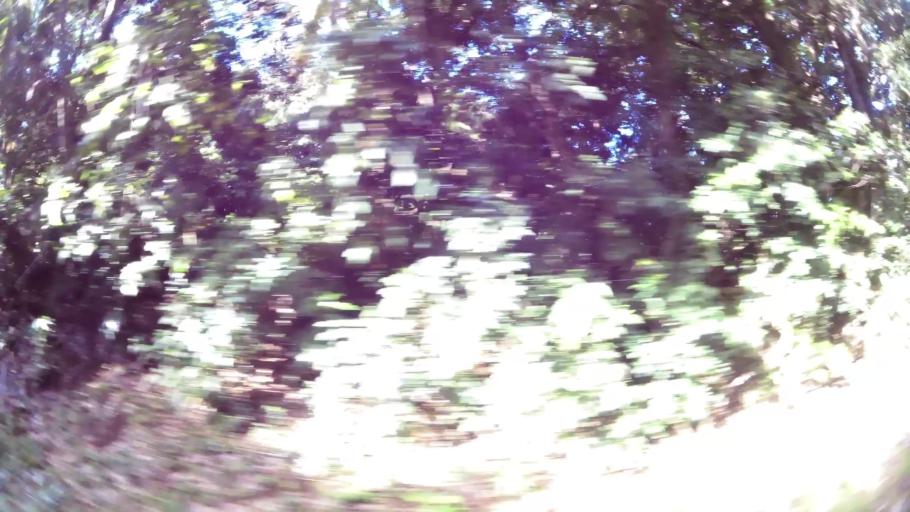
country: DM
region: Saint Andrew
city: Calibishie
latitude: 15.5933
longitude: -61.3739
